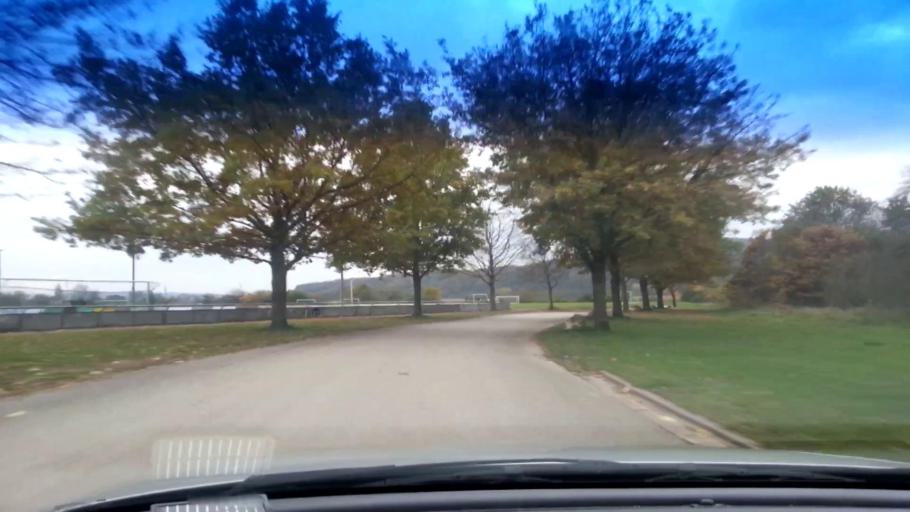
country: DE
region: Bavaria
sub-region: Upper Franconia
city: Kemmern
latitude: 49.9497
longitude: 10.8721
